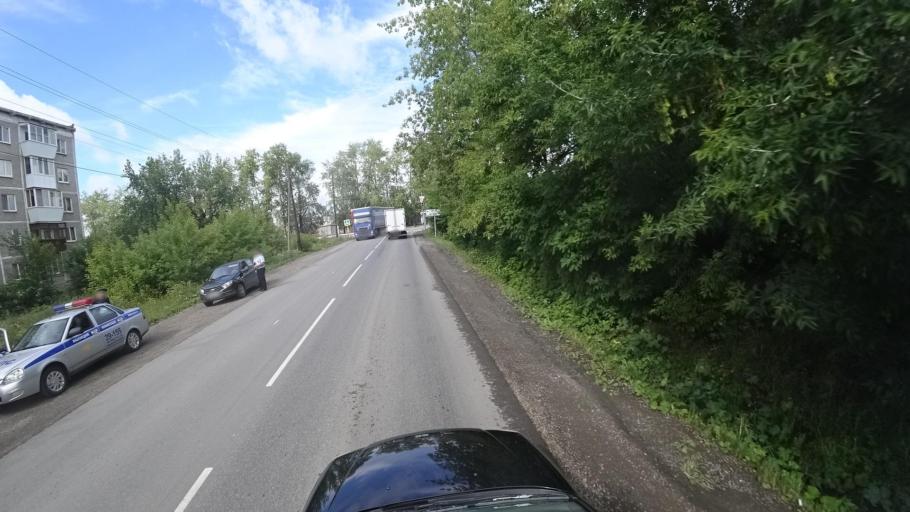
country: RU
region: Sverdlovsk
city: Kamyshlov
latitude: 56.8424
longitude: 62.7205
